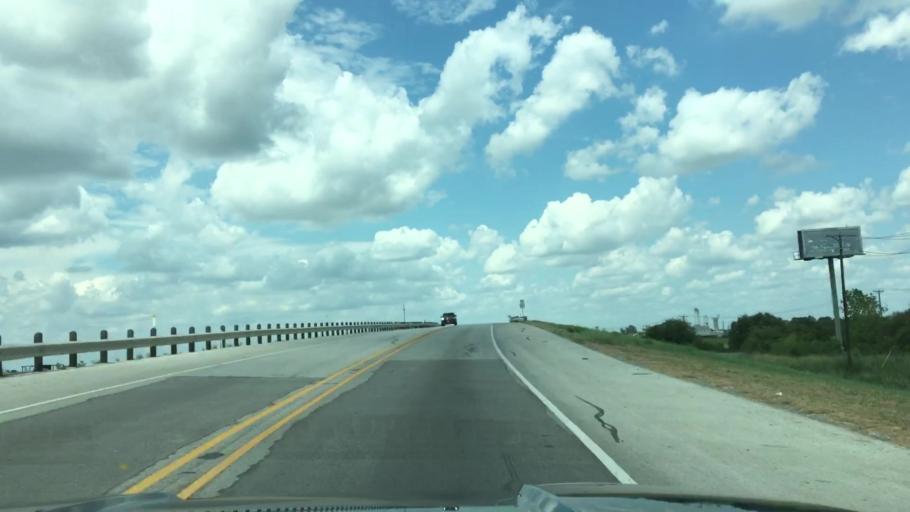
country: US
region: Texas
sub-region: Tarrant County
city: Eagle Mountain
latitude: 32.9421
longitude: -97.4209
